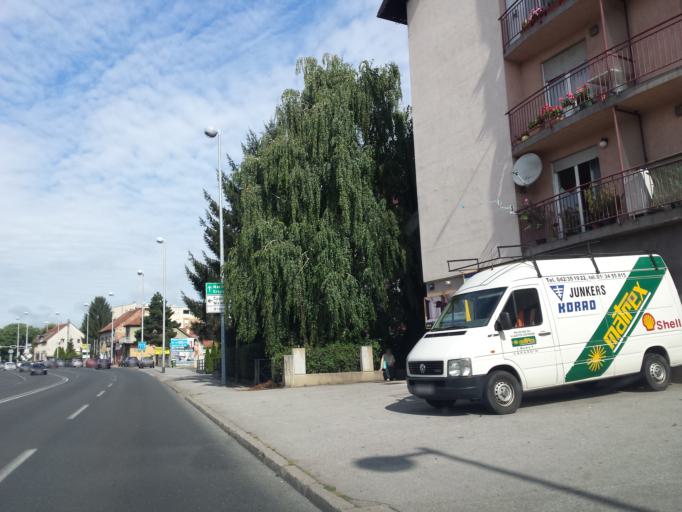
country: HR
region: Grad Zagreb
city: Jankomir
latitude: 45.8125
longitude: 15.9085
